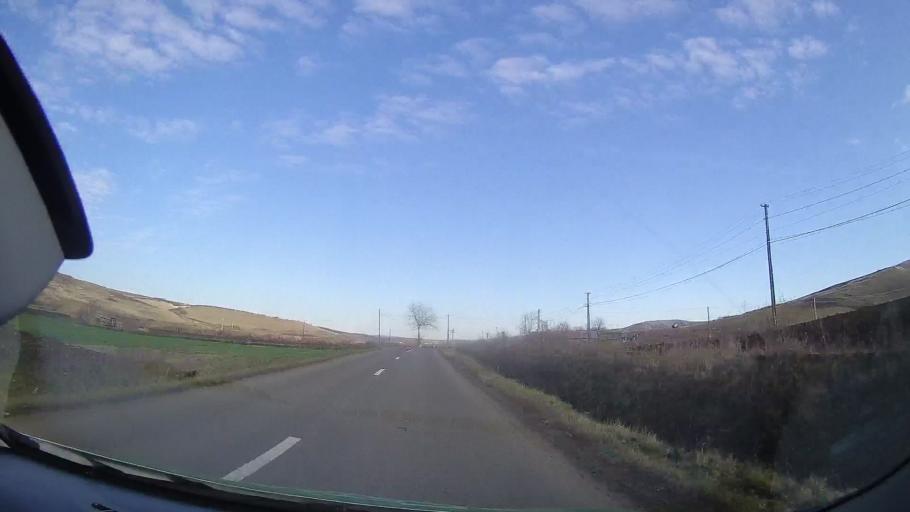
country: RO
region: Mures
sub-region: Comuna Iclanzel
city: Iclanzel
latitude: 46.5291
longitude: 24.2902
